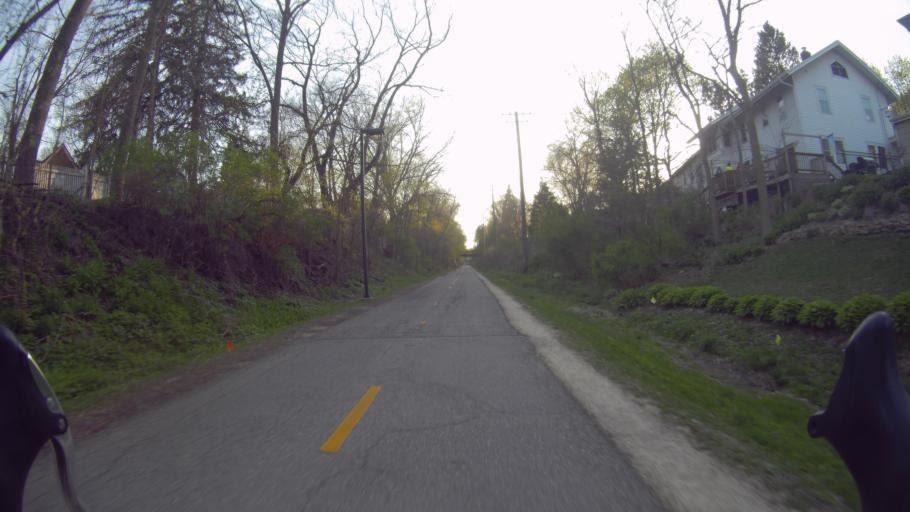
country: US
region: Wisconsin
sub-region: Dane County
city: Madison
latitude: 43.0670
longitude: -89.4172
